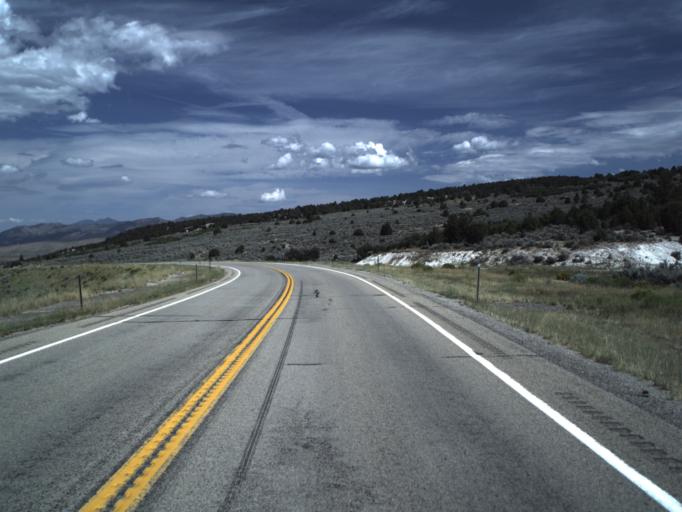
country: US
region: Utah
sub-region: Sanpete County
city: Fairview
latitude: 39.7170
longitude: -111.4709
